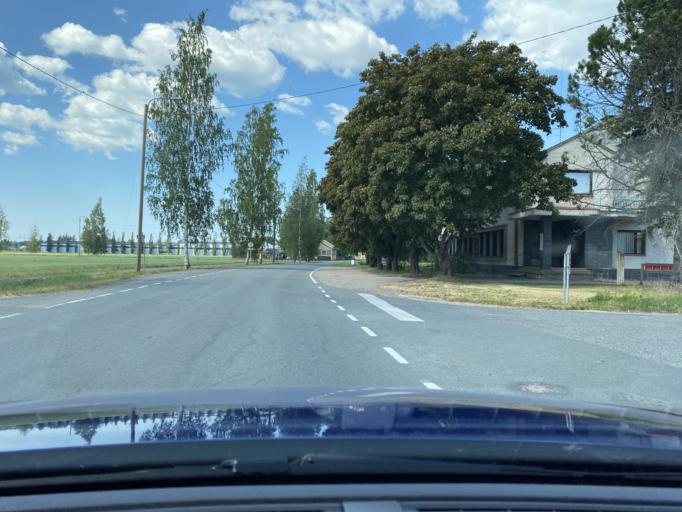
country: FI
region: Satakunta
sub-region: Rauma
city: Eura
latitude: 61.1370
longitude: 22.1264
